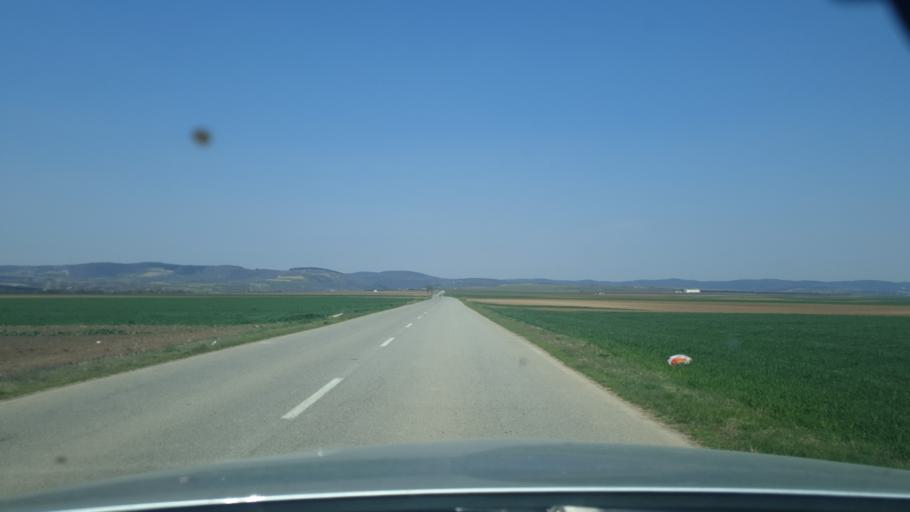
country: RS
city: Vrdnik
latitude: 45.0709
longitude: 19.7698
